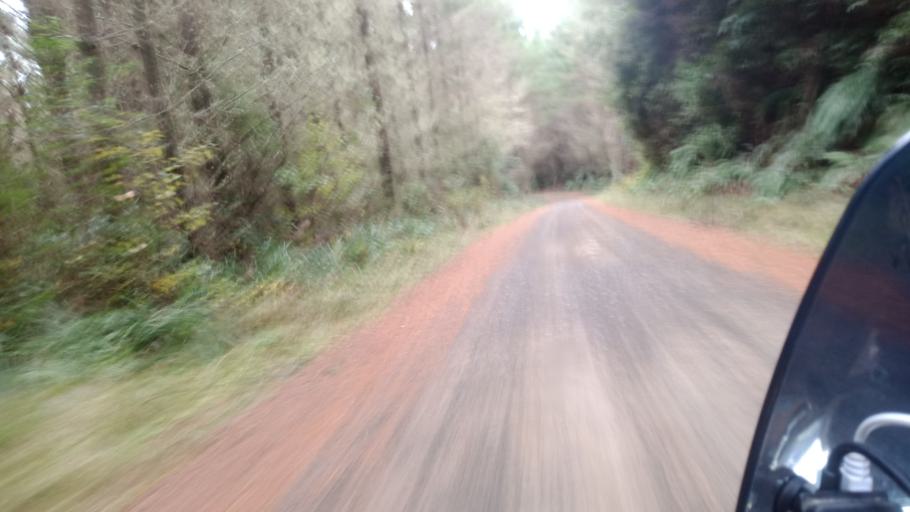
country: NZ
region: Bay of Plenty
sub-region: Whakatane District
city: Murupara
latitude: -38.6552
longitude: 176.6398
